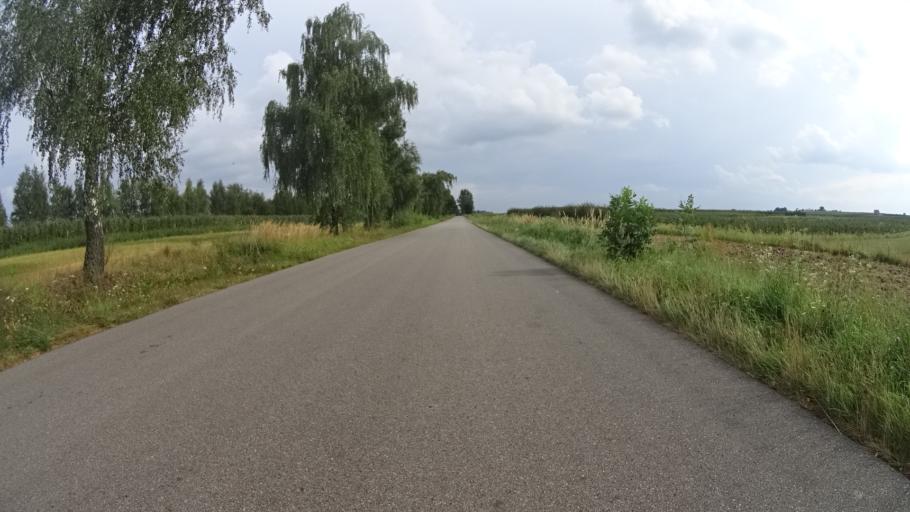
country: PL
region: Masovian Voivodeship
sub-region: Powiat grojecki
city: Goszczyn
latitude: 51.6988
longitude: 20.8557
